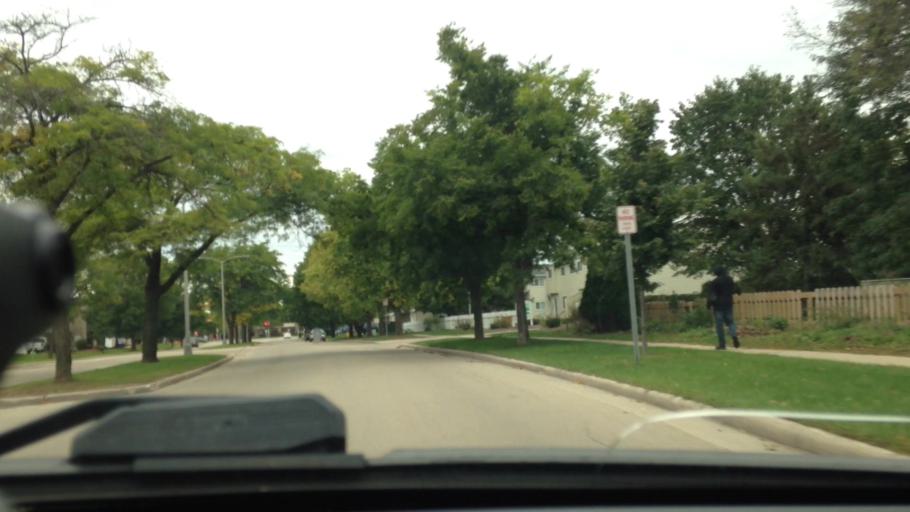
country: US
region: Wisconsin
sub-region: Fond du Lac County
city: North Fond du Lac
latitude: 43.7891
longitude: -88.4728
